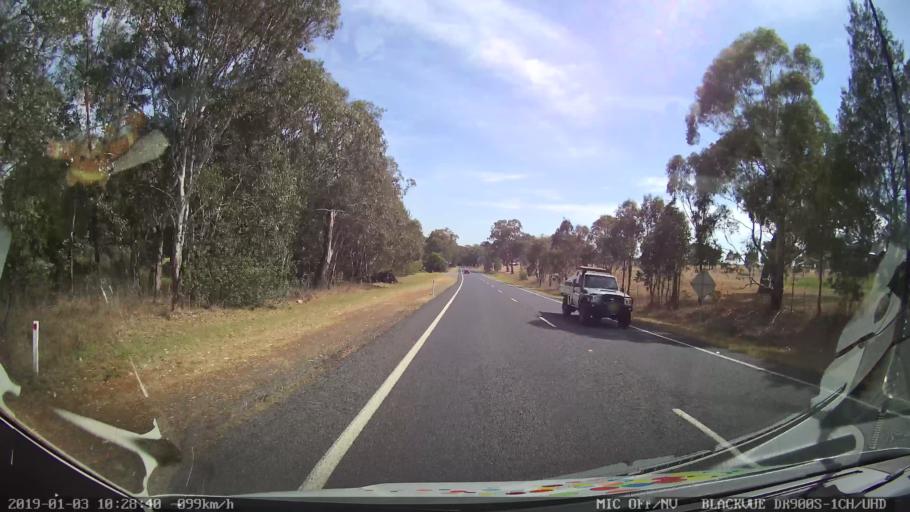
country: AU
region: New South Wales
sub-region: Young
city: Young
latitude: -34.3846
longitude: 148.2594
